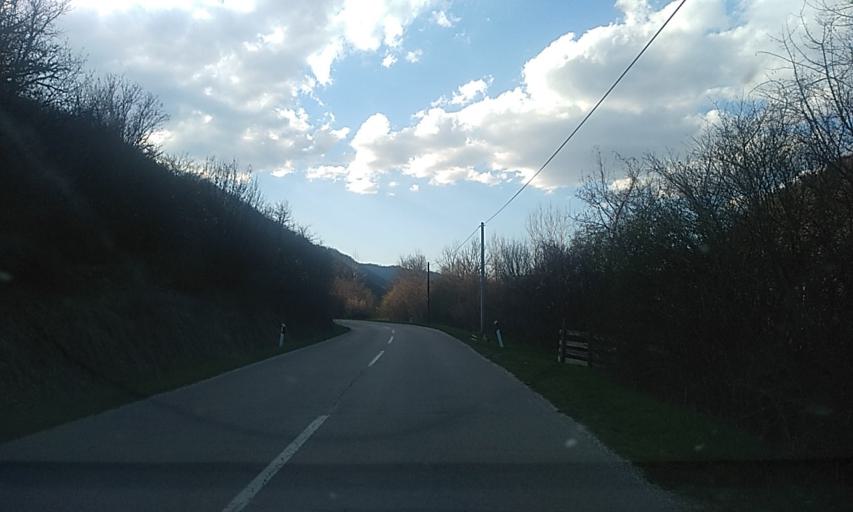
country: RS
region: Central Serbia
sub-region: Pcinjski Okrug
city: Bosilegrad
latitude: 42.4519
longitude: 22.4997
